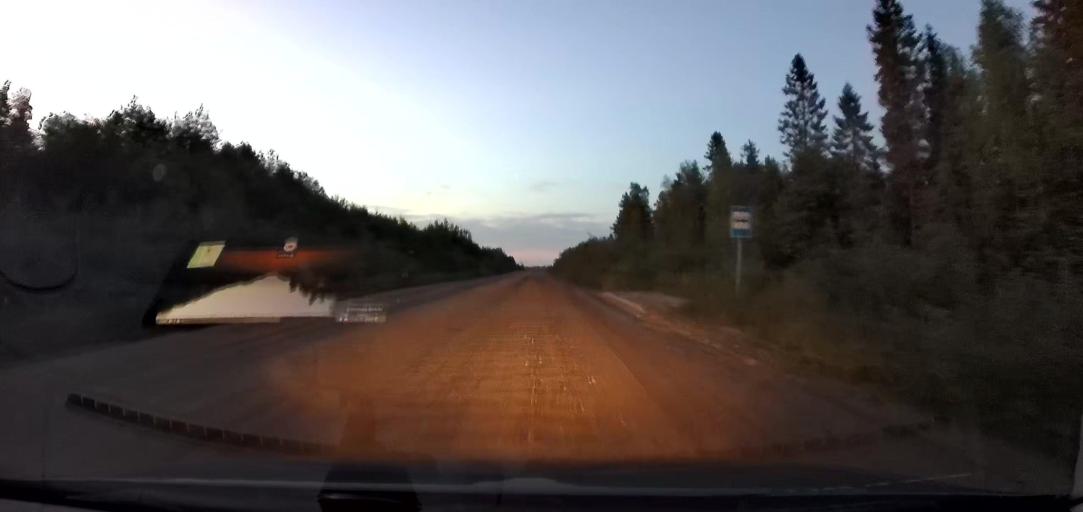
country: RU
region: Arkhangelskaya
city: Kholmogory
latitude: 64.3294
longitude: 41.4349
